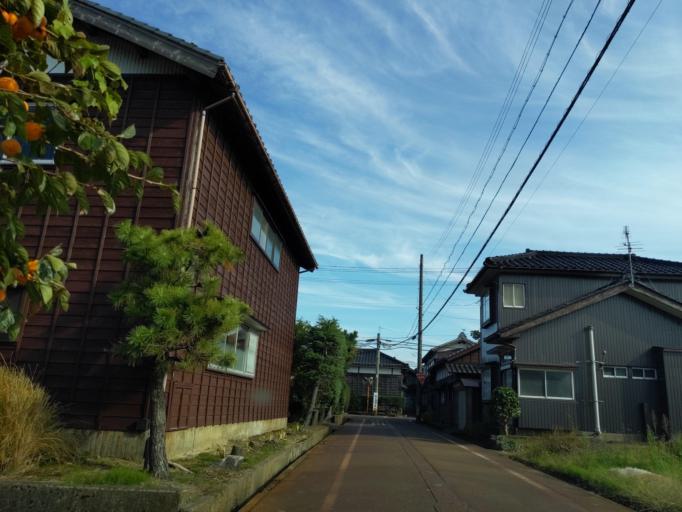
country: JP
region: Niigata
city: Sanjo
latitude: 37.6196
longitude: 138.9436
